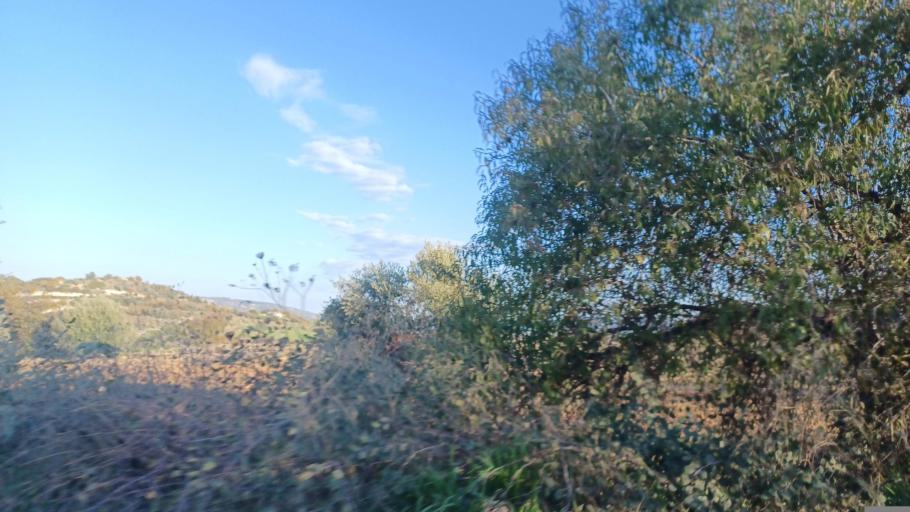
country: CY
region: Pafos
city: Mesogi
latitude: 34.8716
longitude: 32.5799
